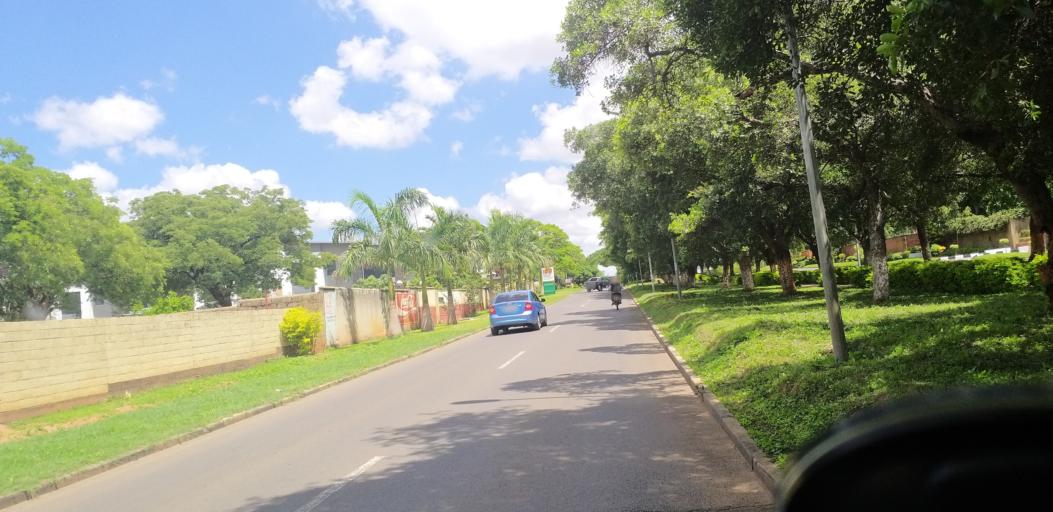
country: ZM
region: Lusaka
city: Lusaka
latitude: -15.4269
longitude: 28.3170
